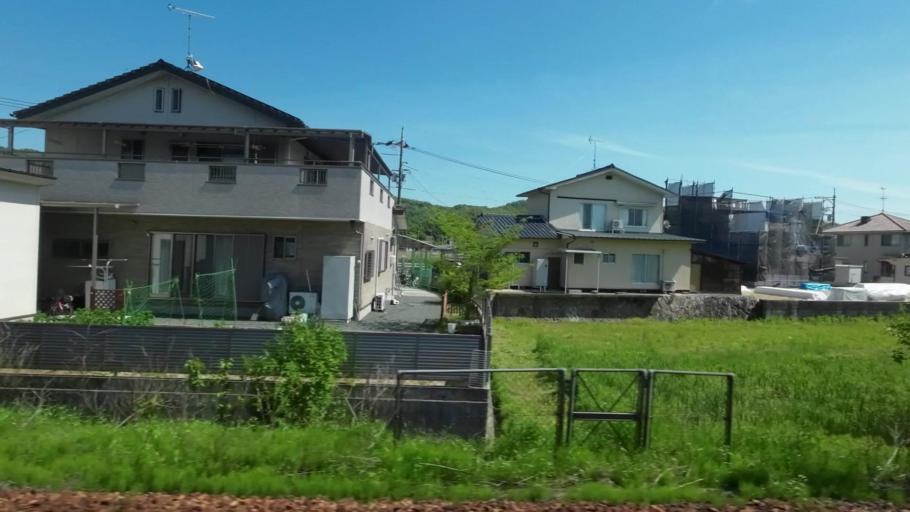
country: JP
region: Hiroshima
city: Onomichi
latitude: 34.4543
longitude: 133.2666
